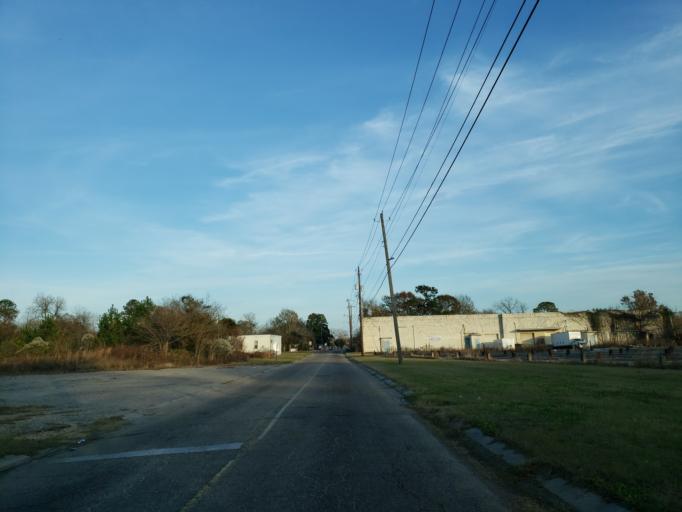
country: US
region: Mississippi
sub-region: Forrest County
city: Hattiesburg
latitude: 31.3357
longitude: -89.2950
